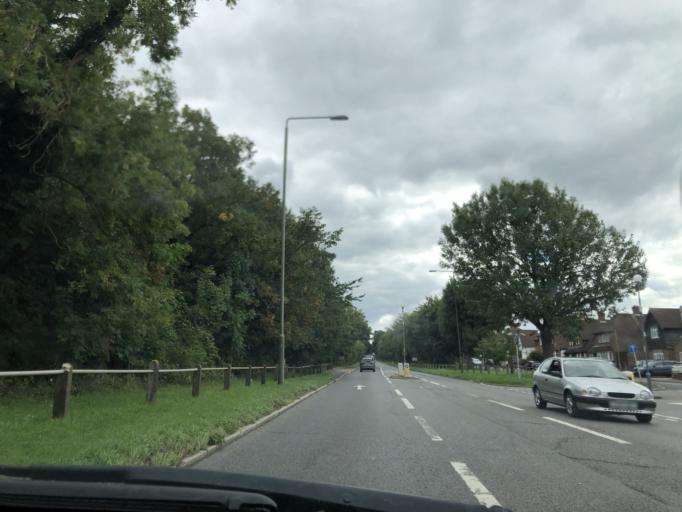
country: GB
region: England
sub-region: Greater London
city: Orpington
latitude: 51.3632
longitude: 0.1138
